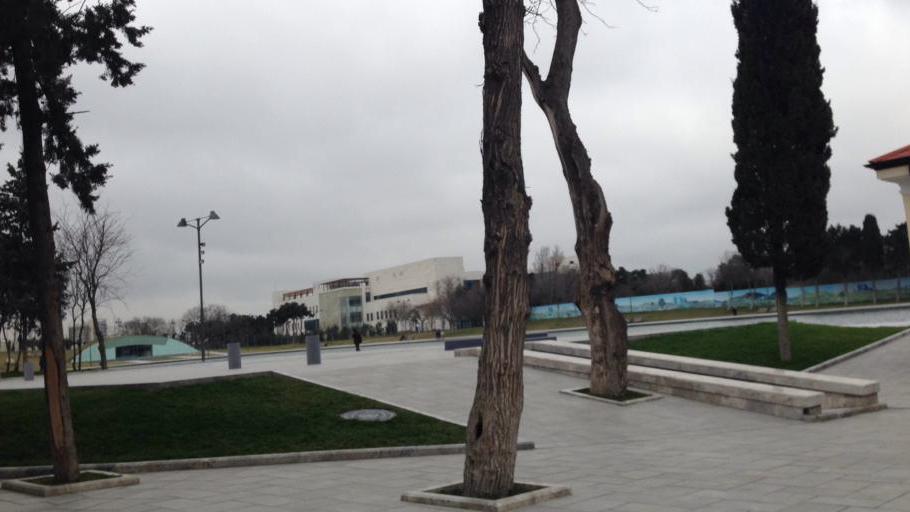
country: AZ
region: Baki
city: Baku
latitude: 40.3920
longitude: 49.8471
